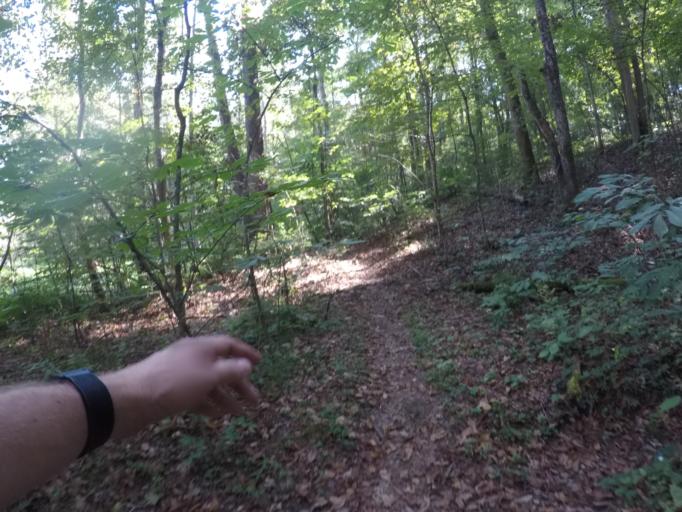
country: US
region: Ohio
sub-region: Lawrence County
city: Ironton
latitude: 38.6247
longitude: -82.6142
